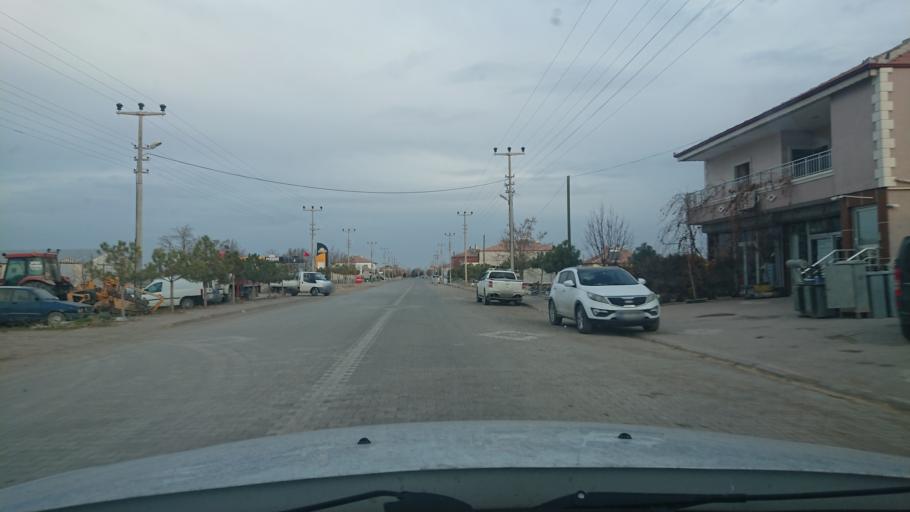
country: TR
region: Aksaray
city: Yesilova
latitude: 38.3373
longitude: 33.7510
